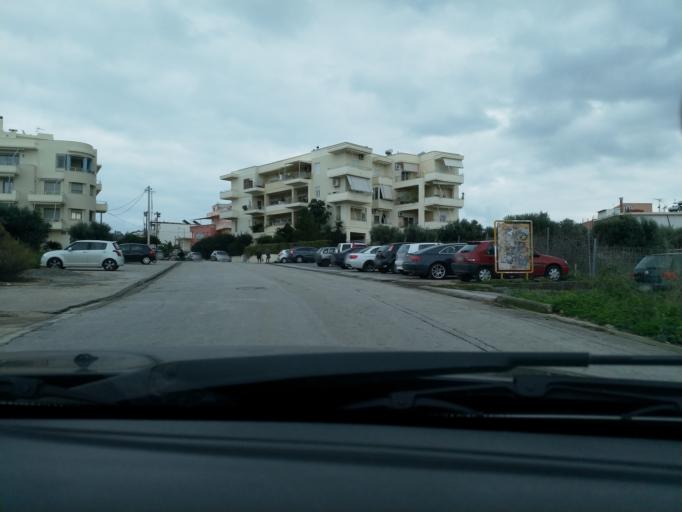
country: GR
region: Crete
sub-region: Nomos Chanias
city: Chania
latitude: 35.5113
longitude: 24.0385
